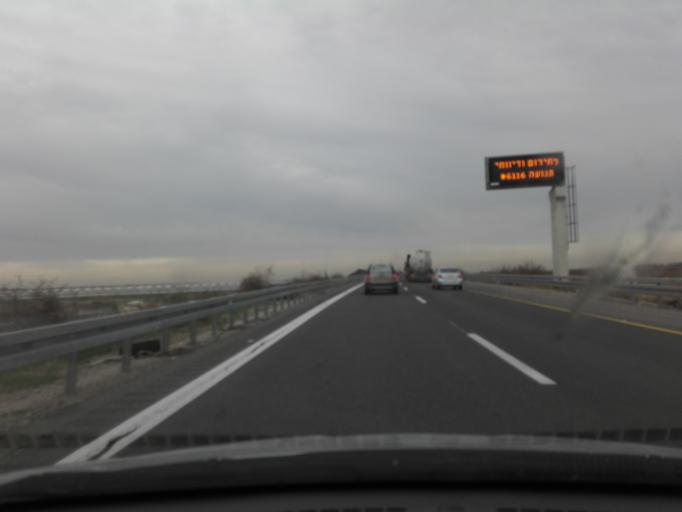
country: IL
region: Central District
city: Mazkeret Batya
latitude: 31.8278
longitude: 34.8520
